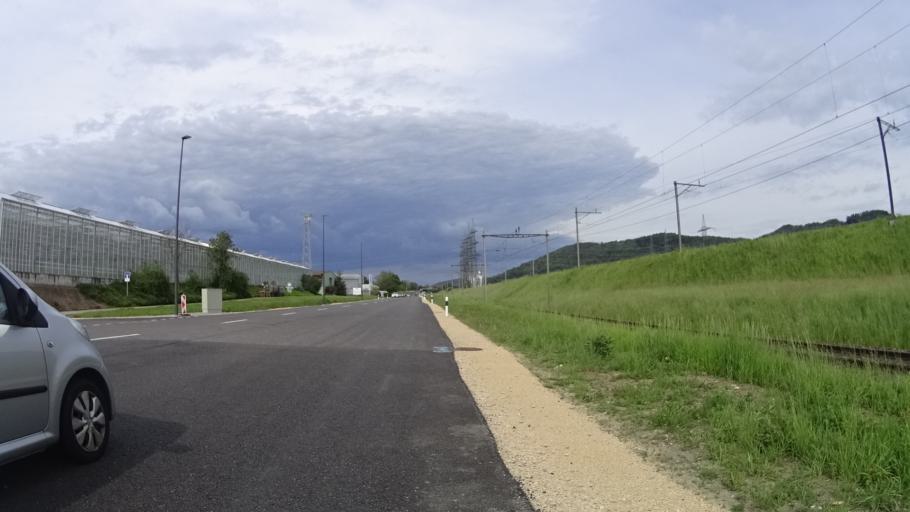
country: CH
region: Aargau
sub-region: Bezirk Laufenburg
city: Kaisten
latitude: 47.5510
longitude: 8.0393
